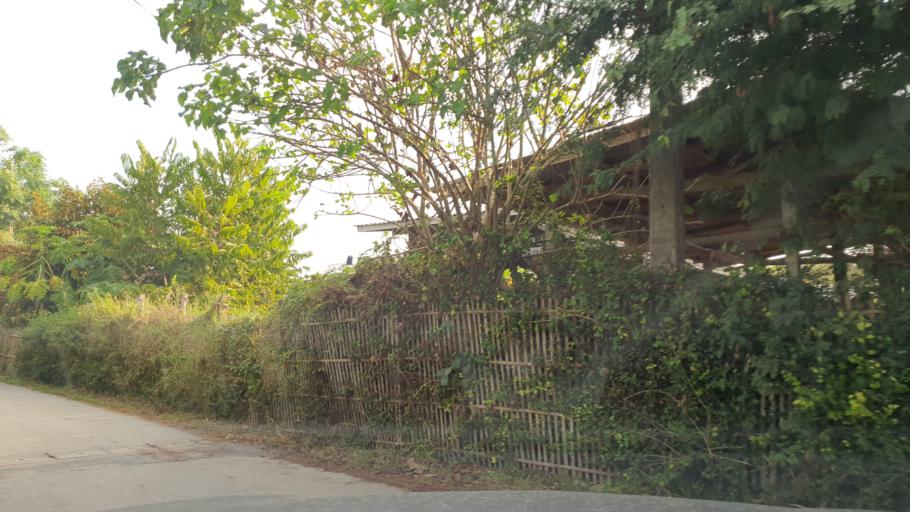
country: TH
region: Chiang Mai
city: San Kamphaeng
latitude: 18.7360
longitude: 99.1082
